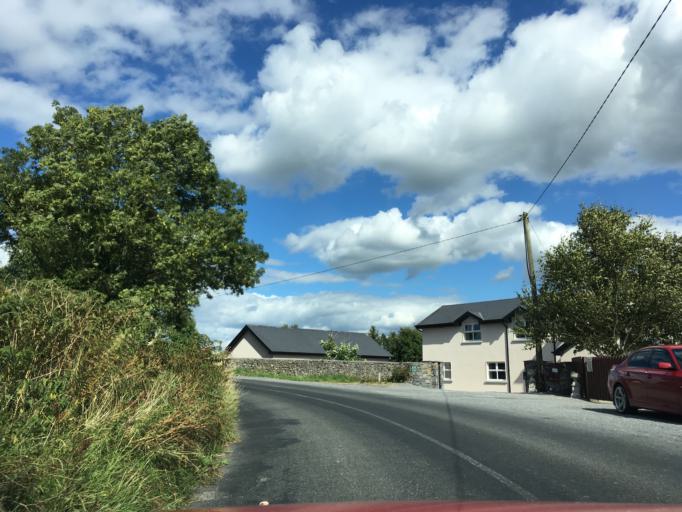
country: IE
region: Munster
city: Cahir
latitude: 52.4562
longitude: -7.9461
